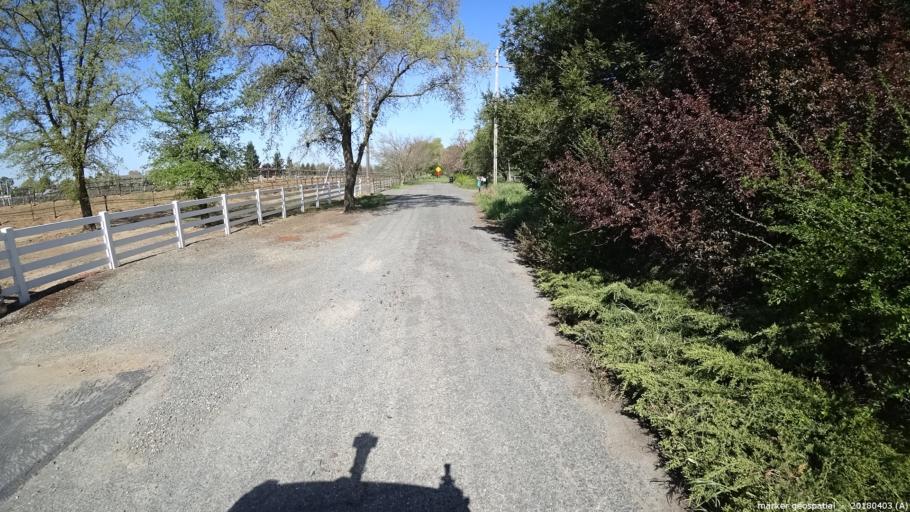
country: US
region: California
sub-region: Sacramento County
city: Wilton
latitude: 38.4369
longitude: -121.2268
